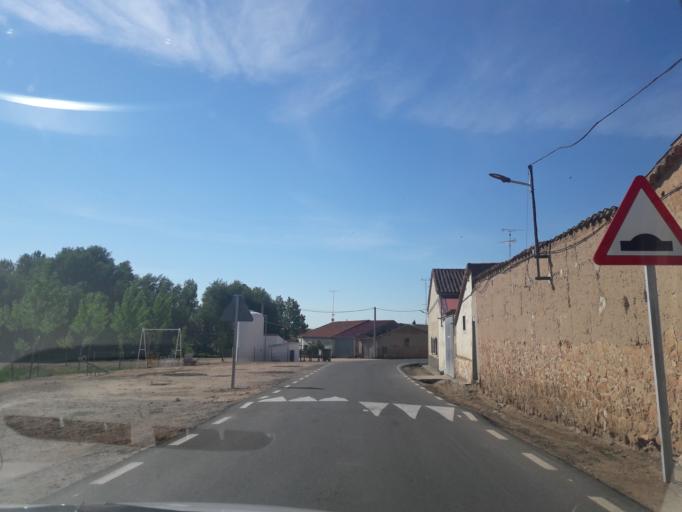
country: ES
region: Castille and Leon
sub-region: Provincia de Salamanca
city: Espino de la Orbada
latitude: 41.1077
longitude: -5.4229
